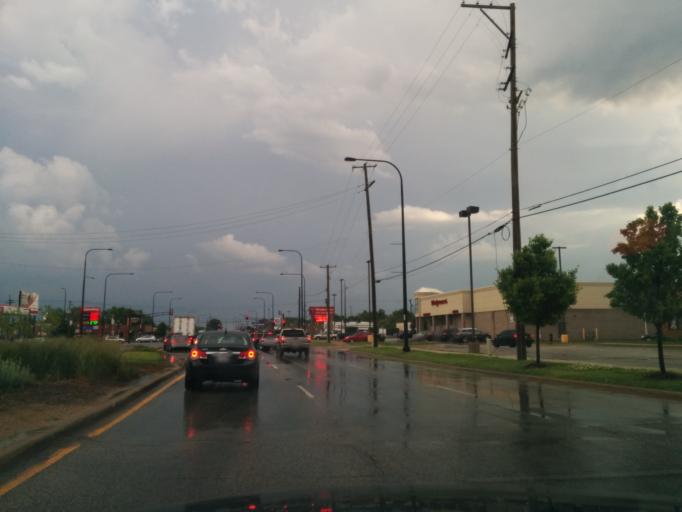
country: US
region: Illinois
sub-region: Cook County
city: Bridgeview
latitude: 41.7496
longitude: -87.7999
